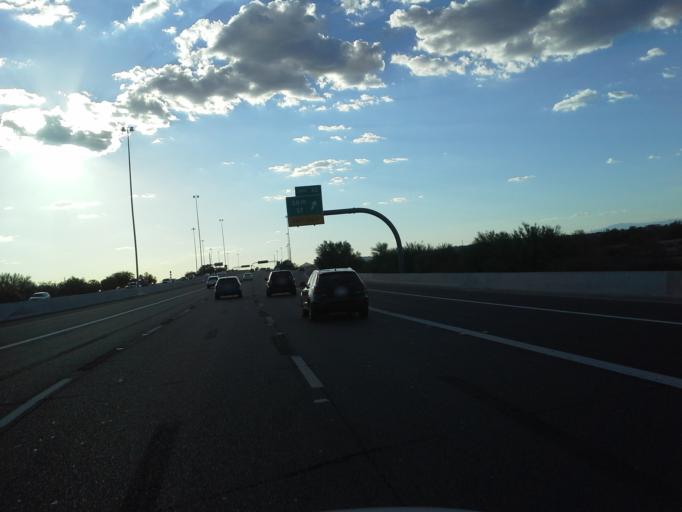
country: US
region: Arizona
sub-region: Maricopa County
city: Paradise Valley
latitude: 33.6648
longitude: -111.9532
